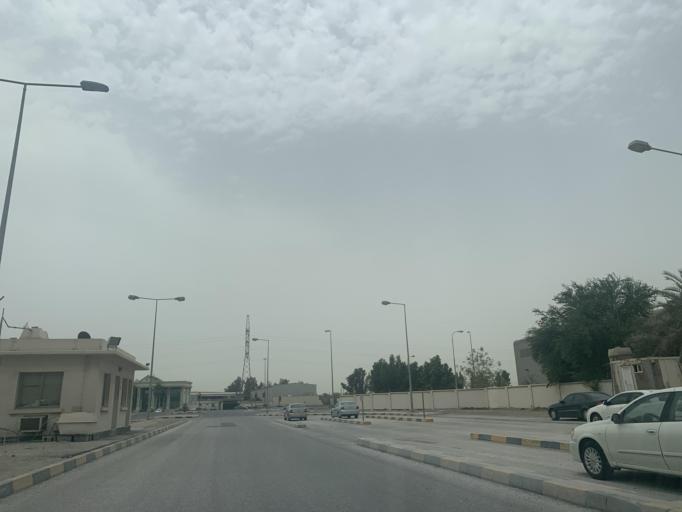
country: BH
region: Northern
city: Sitrah
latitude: 26.1782
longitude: 50.6154
